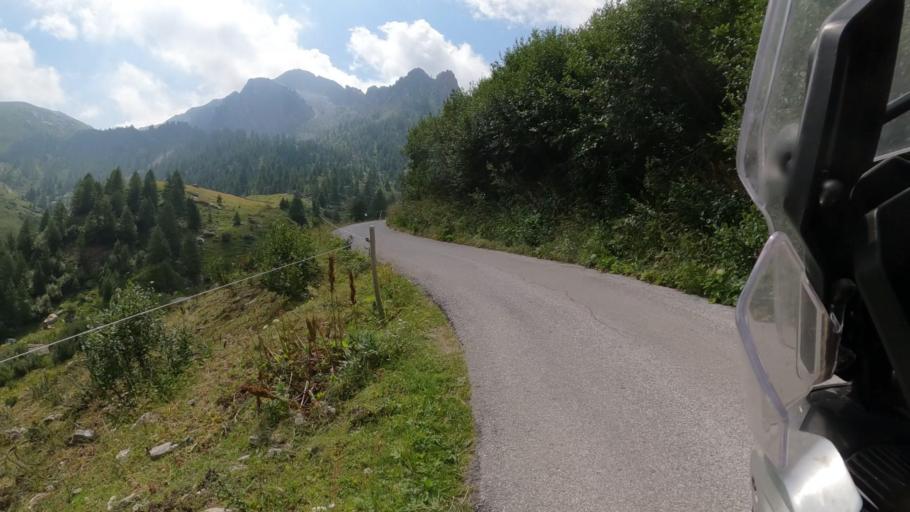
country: IT
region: Piedmont
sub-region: Provincia di Cuneo
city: Marmora
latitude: 44.4006
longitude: 7.1059
